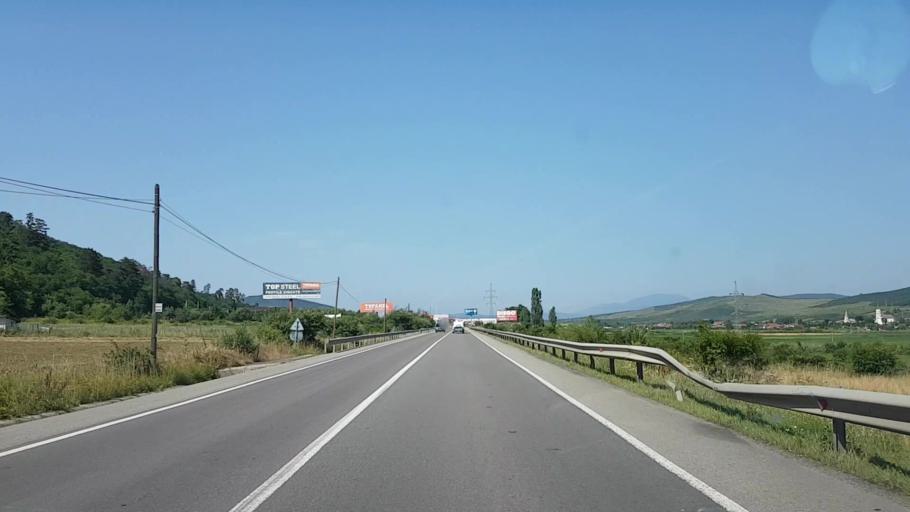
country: RO
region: Bistrita-Nasaud
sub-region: Comuna Sieu-Magherus
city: Sieu-Magherus
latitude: 47.0654
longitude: 24.4189
